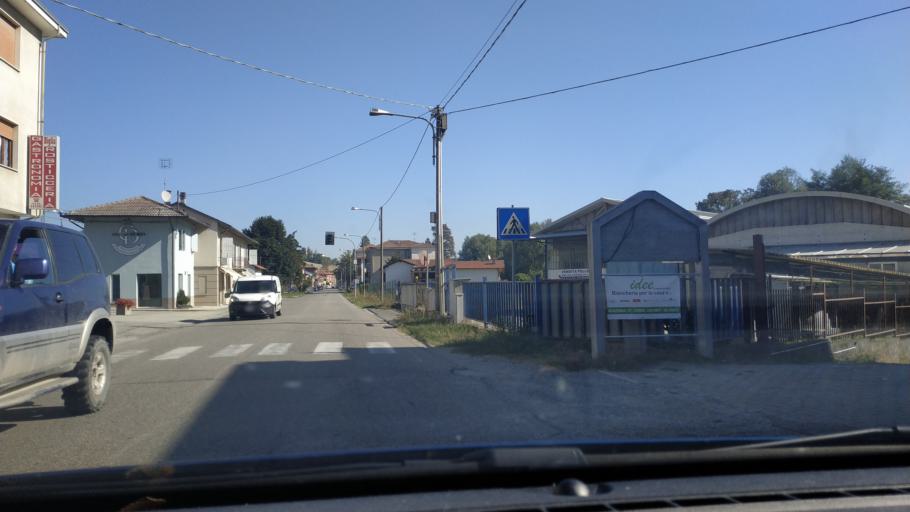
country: IT
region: Piedmont
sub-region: Provincia di Alessandria
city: Cerrina
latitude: 45.1114
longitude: 8.2092
